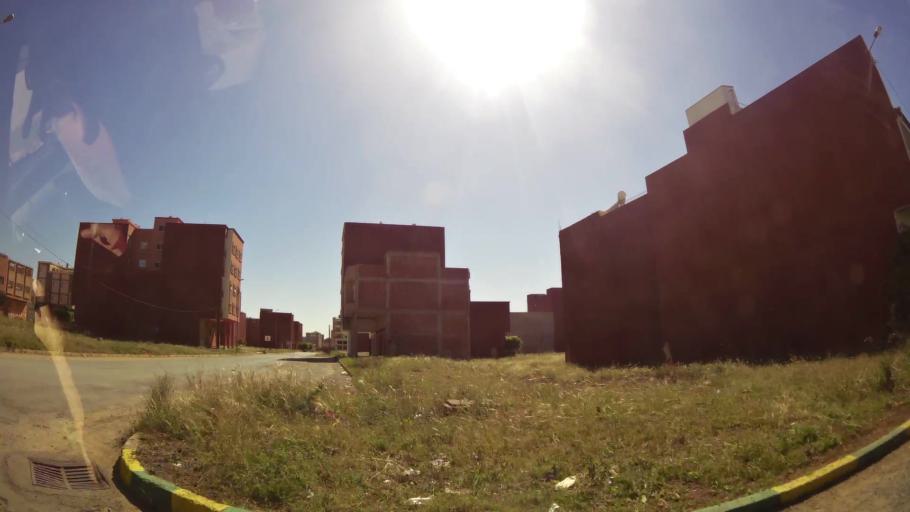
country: MA
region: Oriental
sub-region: Berkane-Taourirt
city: Berkane
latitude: 34.9436
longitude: -2.3285
